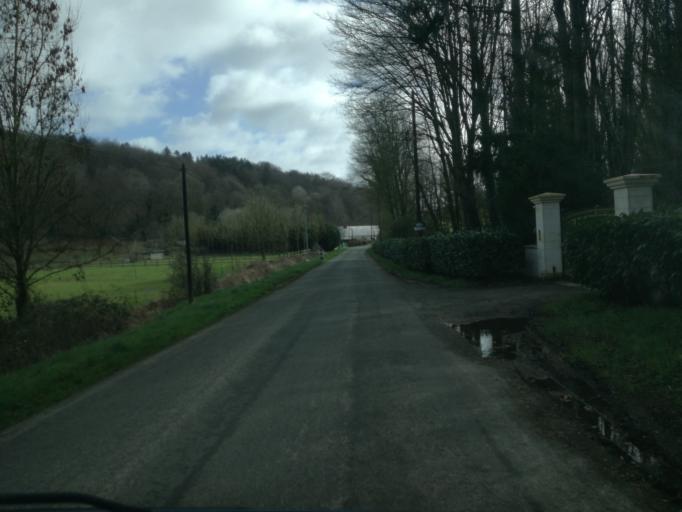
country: FR
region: Haute-Normandie
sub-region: Departement de la Seine-Maritime
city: Bretteville-du-Grand-Caux
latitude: 49.7003
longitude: 0.4566
